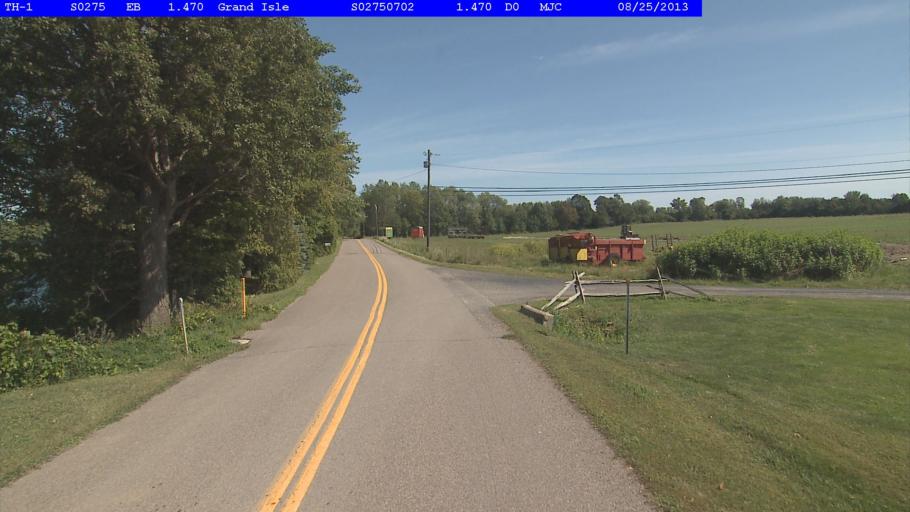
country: US
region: New York
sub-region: Clinton County
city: Cumberland Head
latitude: 44.7212
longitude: -73.3396
